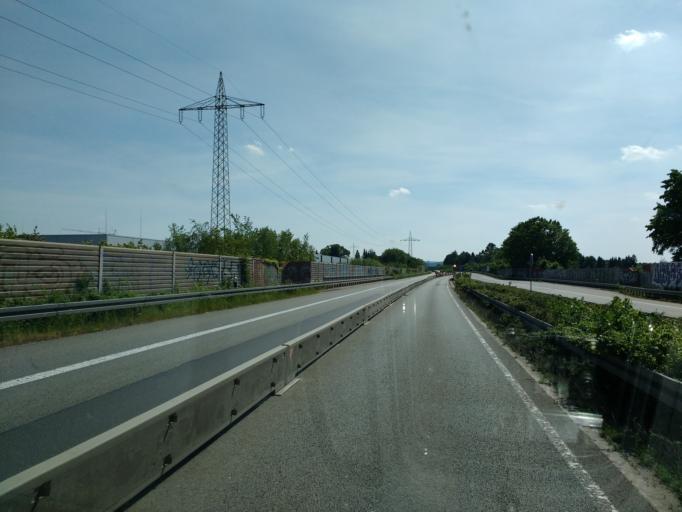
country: DE
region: Lower Saxony
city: Belm
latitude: 52.2829
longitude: 8.1086
